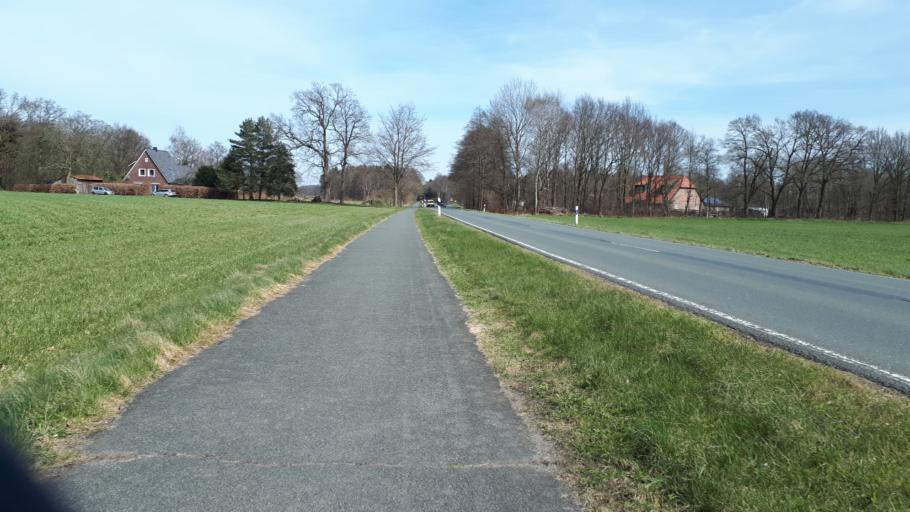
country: DE
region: Lower Saxony
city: Wardenburg
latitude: 53.0387
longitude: 8.1641
